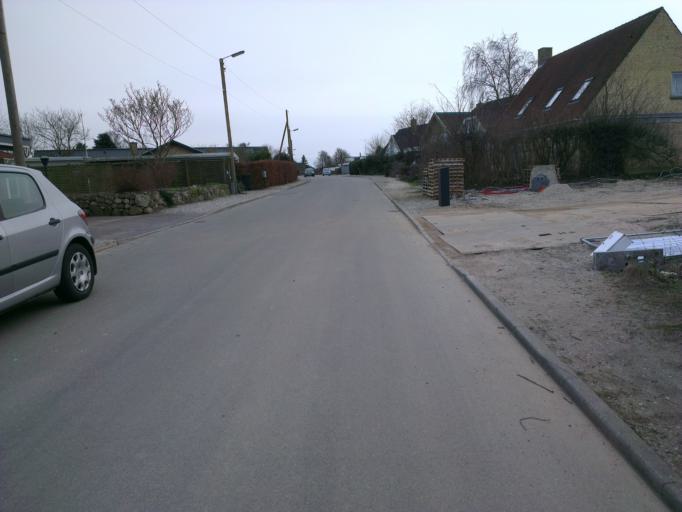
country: DK
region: Capital Region
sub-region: Frederikssund Kommune
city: Frederikssund
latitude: 55.8266
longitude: 12.0649
